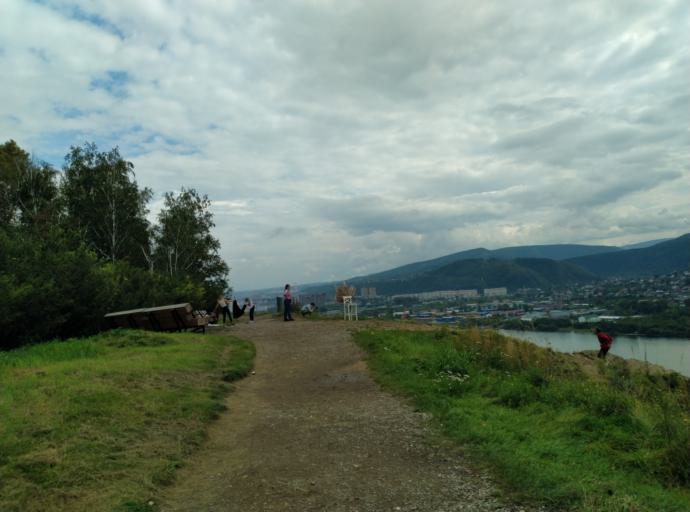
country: RU
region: Krasnoyarskiy
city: Krasnoyarsk
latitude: 55.9828
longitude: 92.7582
